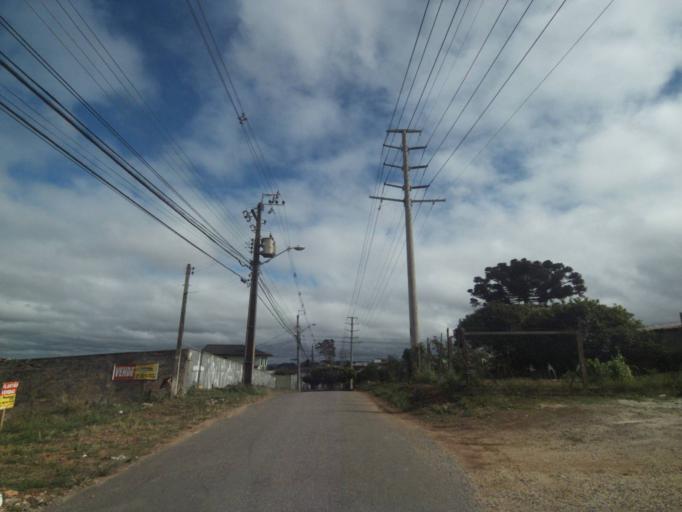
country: BR
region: Parana
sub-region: Sao Jose Dos Pinhais
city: Sao Jose dos Pinhais
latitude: -25.5223
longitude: -49.3024
